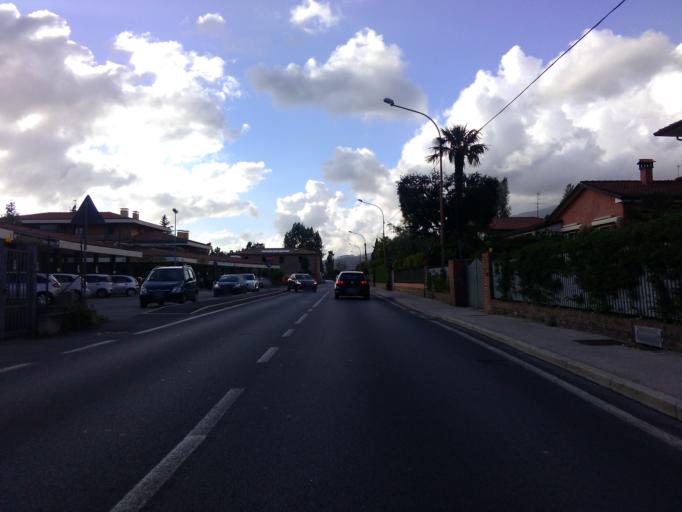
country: IT
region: Tuscany
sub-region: Provincia di Lucca
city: Pietrasanta
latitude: 43.9644
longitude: 10.2233
